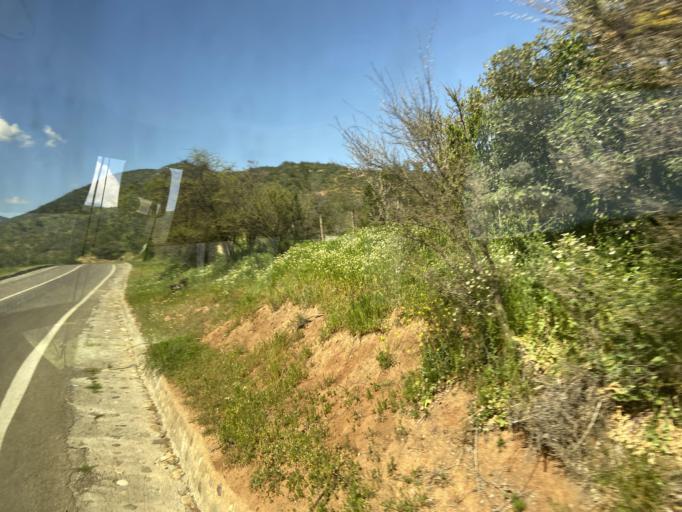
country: CL
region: Valparaiso
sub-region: Provincia de Marga Marga
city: Villa Alemana
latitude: -33.1873
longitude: -71.2958
